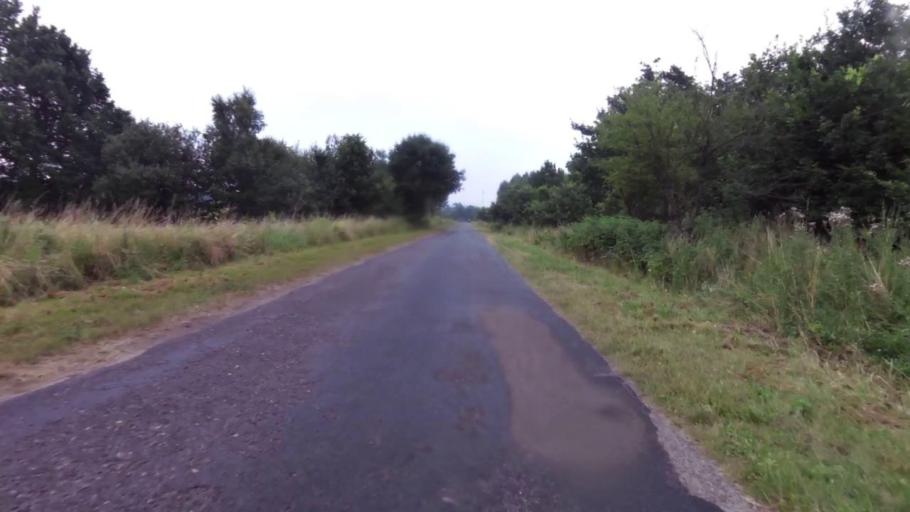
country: PL
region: West Pomeranian Voivodeship
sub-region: Powiat lobeski
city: Wegorzyno
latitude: 53.5342
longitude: 15.6614
